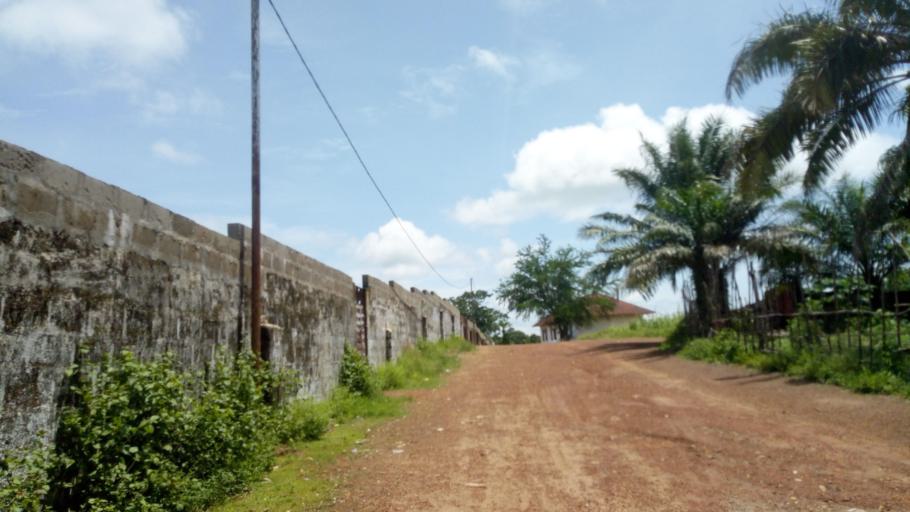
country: SL
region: Northern Province
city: Magburaka
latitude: 8.7182
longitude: -11.9580
